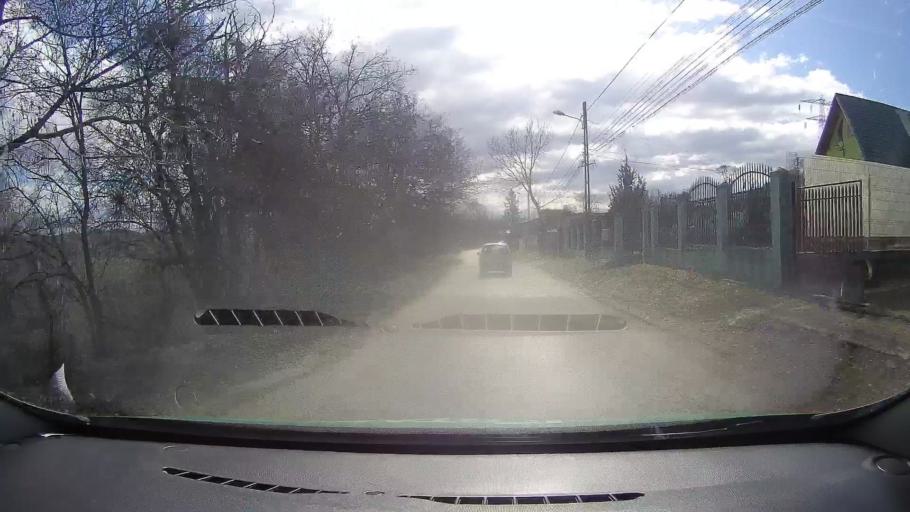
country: RO
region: Dambovita
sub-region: Oras Pucioasa
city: Pucioasa
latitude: 45.0656
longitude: 25.4243
